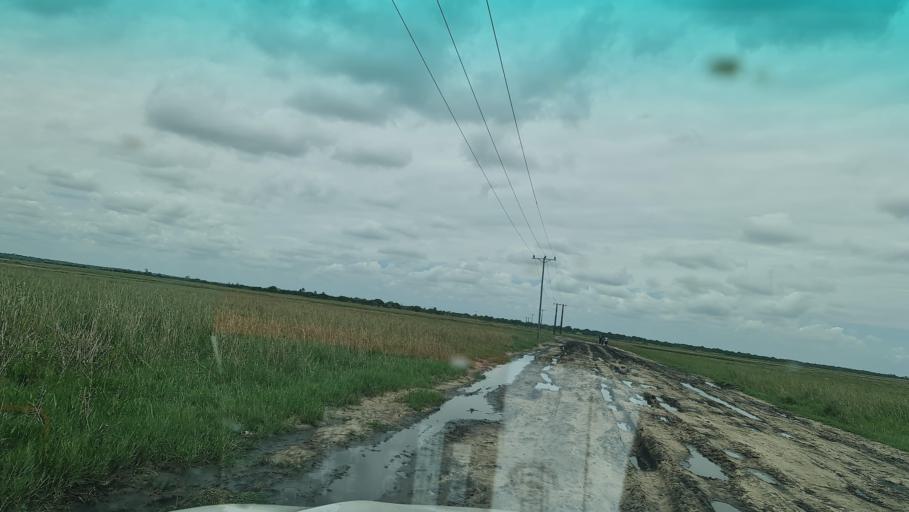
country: MZ
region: Maputo City
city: Maputo
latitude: -25.7123
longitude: 32.7028
